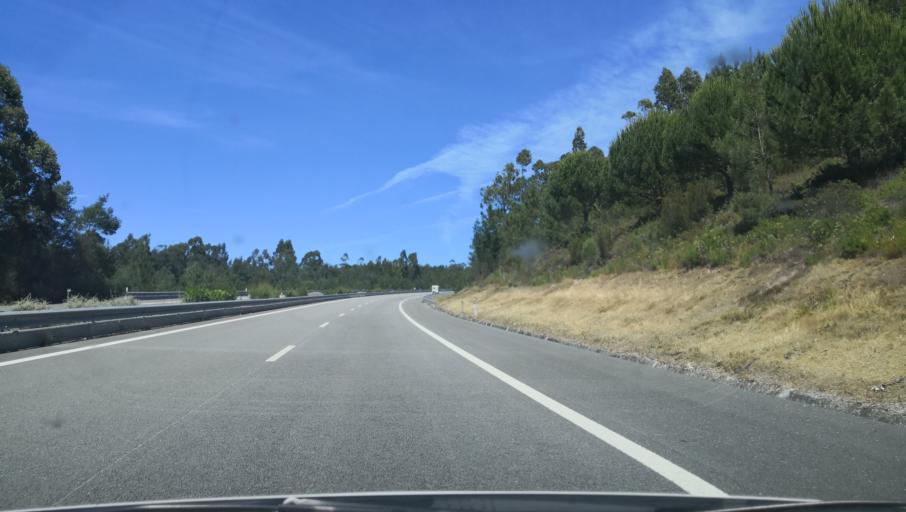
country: PT
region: Coimbra
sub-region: Montemor-O-Velho
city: Arazede
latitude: 40.2447
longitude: -8.6573
